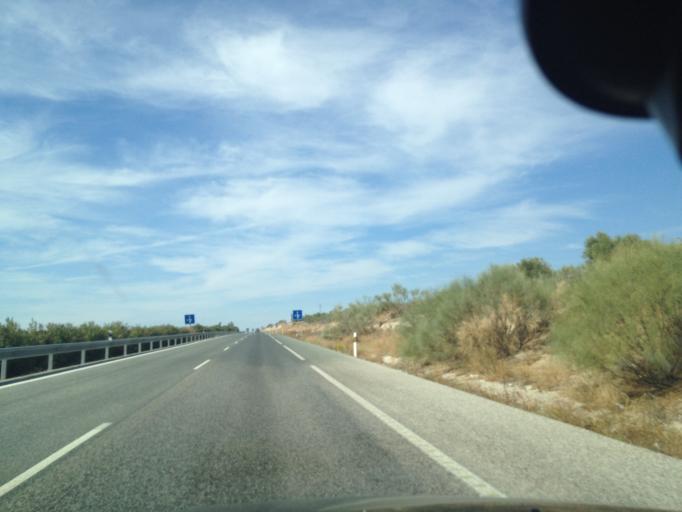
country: ES
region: Andalusia
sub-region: Provincia de Sevilla
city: La Puebla de Cazalla
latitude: 37.2315
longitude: -5.2482
